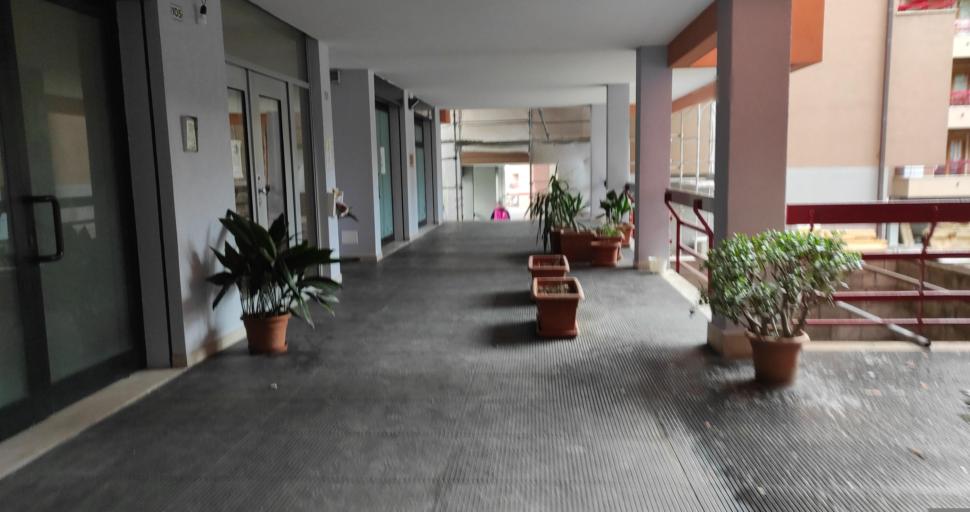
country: IT
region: The Marches
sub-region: Provincia di Macerata
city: Villa Potenza
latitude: 43.2991
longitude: 13.4268
